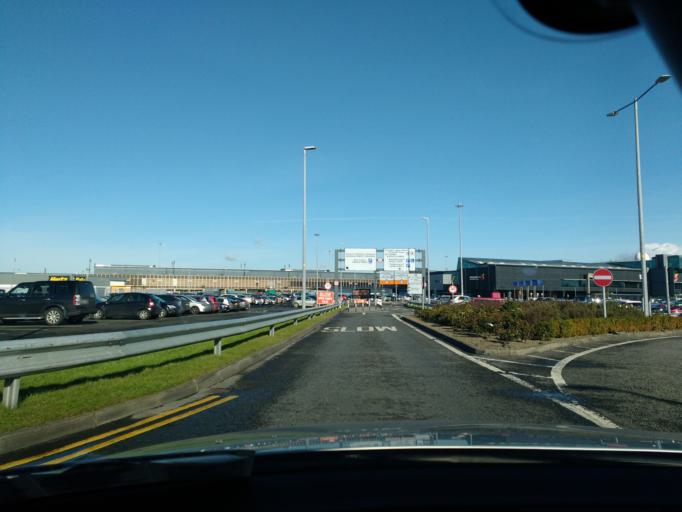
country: IE
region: Munster
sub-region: An Clar
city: Shannon
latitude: 52.6913
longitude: -8.9240
